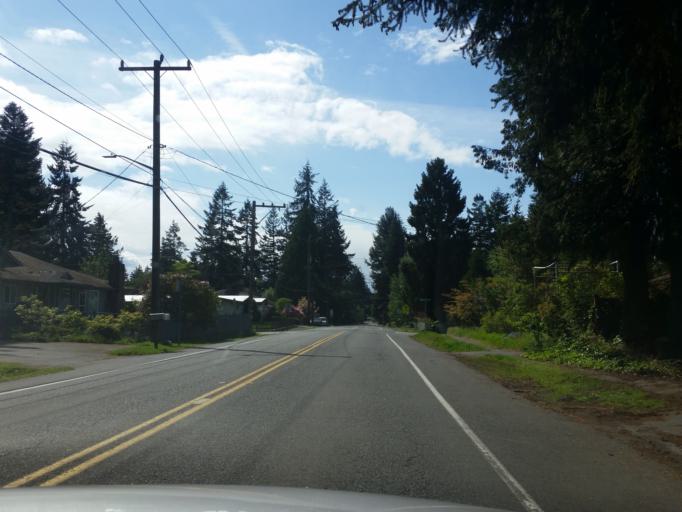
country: US
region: Washington
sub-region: Snohomish County
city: Esperance
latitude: 47.7742
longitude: -122.3528
